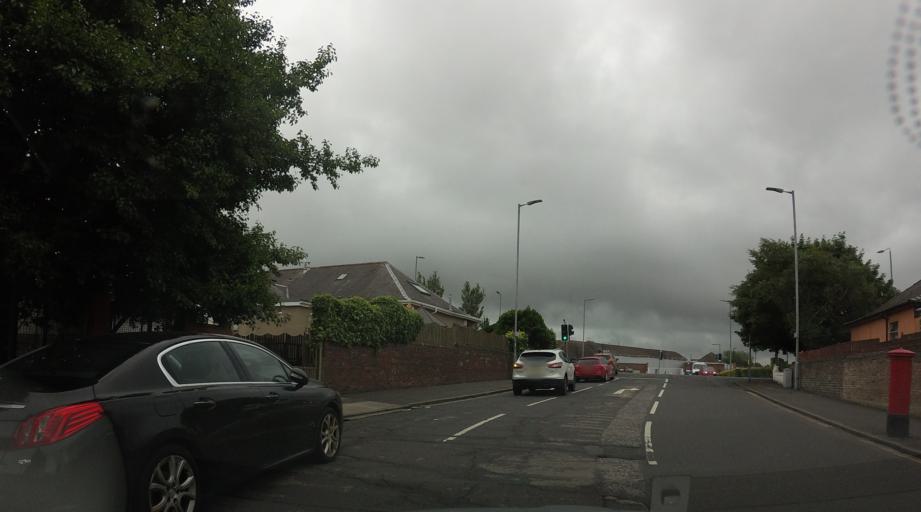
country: GB
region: Scotland
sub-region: South Ayrshire
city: Prestwick
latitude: 55.4692
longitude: -4.6101
